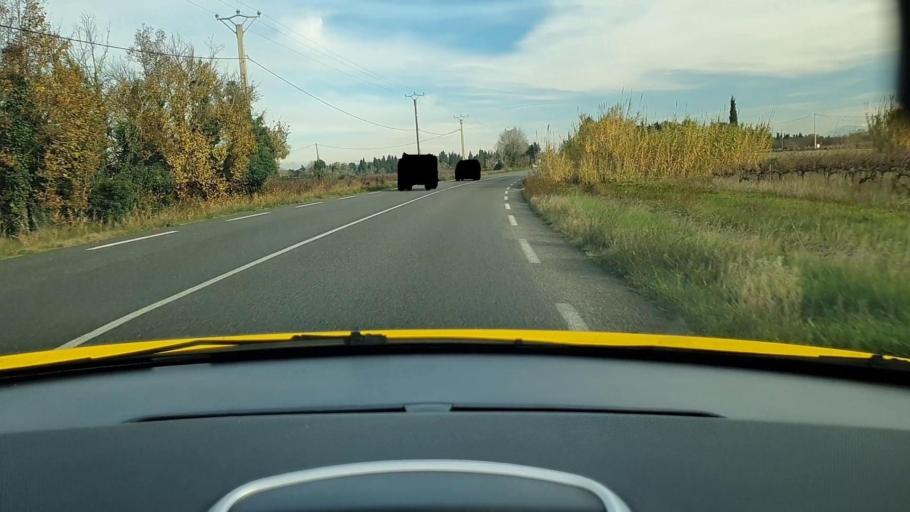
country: FR
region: Languedoc-Roussillon
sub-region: Departement du Gard
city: Beaucaire
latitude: 43.7781
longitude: 4.6220
